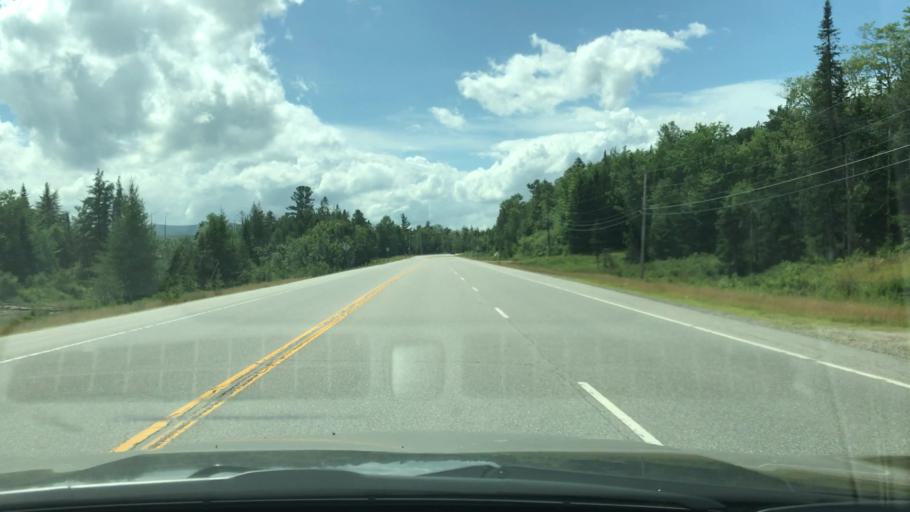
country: US
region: New Hampshire
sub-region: Coos County
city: Jefferson
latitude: 44.3579
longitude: -71.3450
